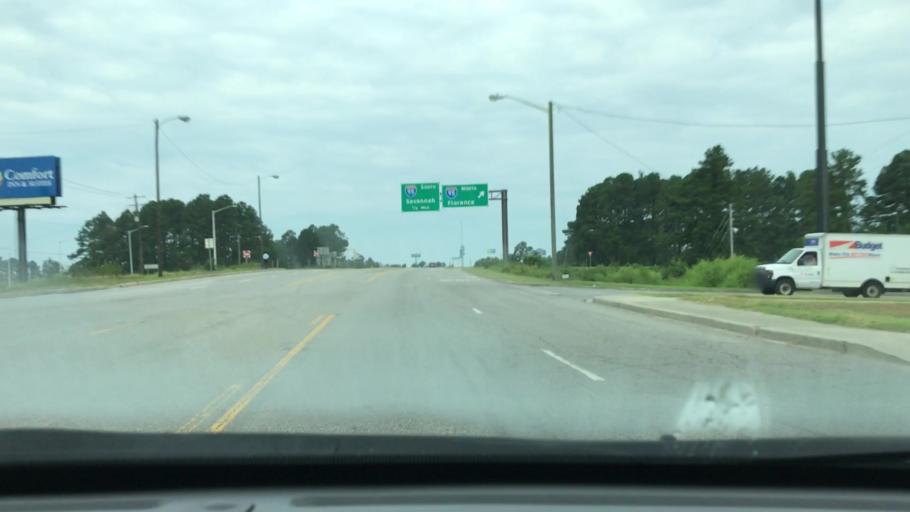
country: US
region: South Carolina
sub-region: Colleton County
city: Walterboro
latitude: 32.8796
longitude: -80.7132
